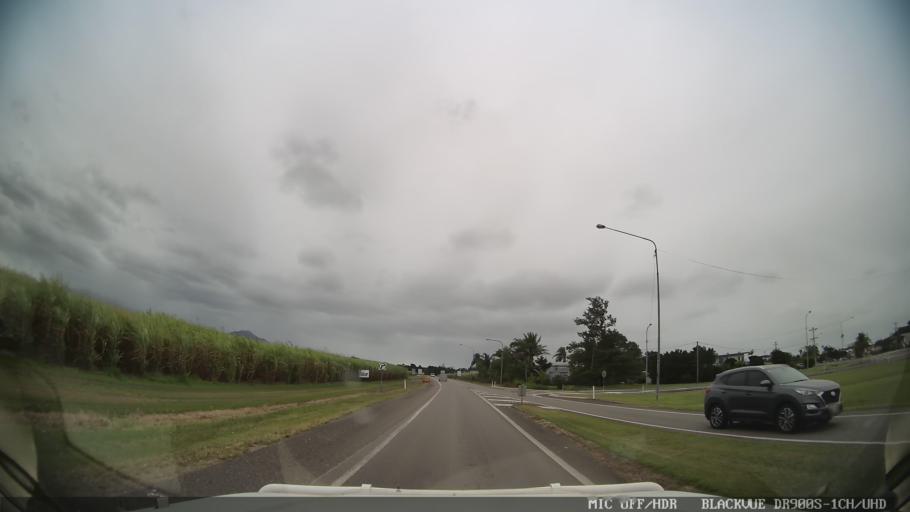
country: AU
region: Queensland
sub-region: Hinchinbrook
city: Ingham
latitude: -18.6406
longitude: 146.1639
